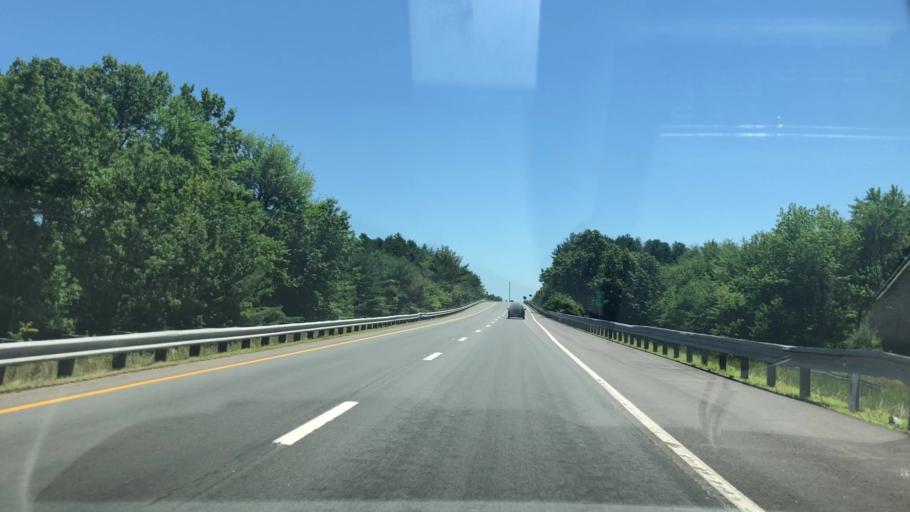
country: US
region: New Hampshire
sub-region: Hillsborough County
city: Manchester
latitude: 42.9596
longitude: -71.4114
